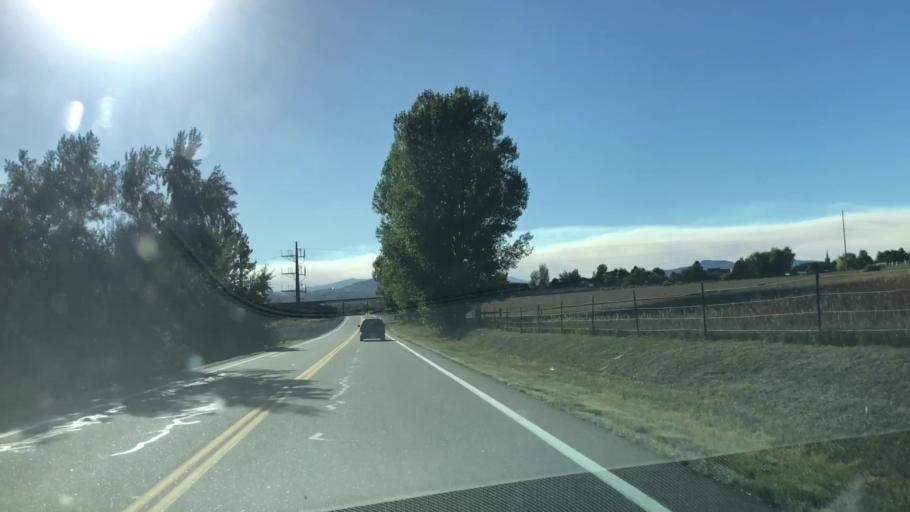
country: US
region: Colorado
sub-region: Larimer County
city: Fort Collins
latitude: 40.4947
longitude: -105.0452
